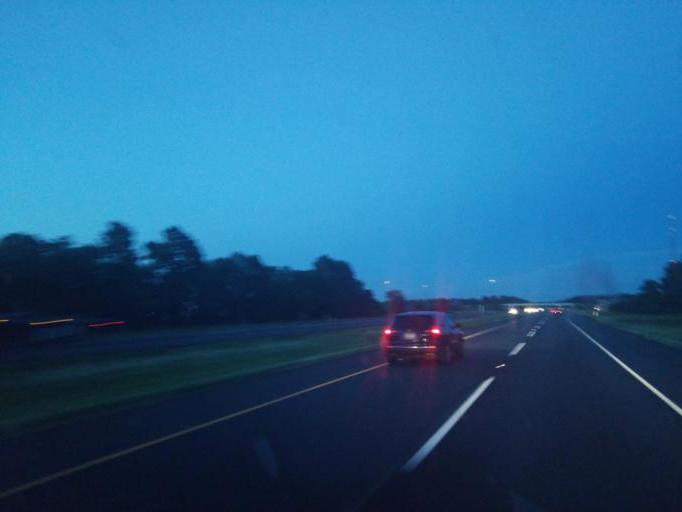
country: US
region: Indiana
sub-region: Saint Joseph County
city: Granger
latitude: 41.7311
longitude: -86.0691
